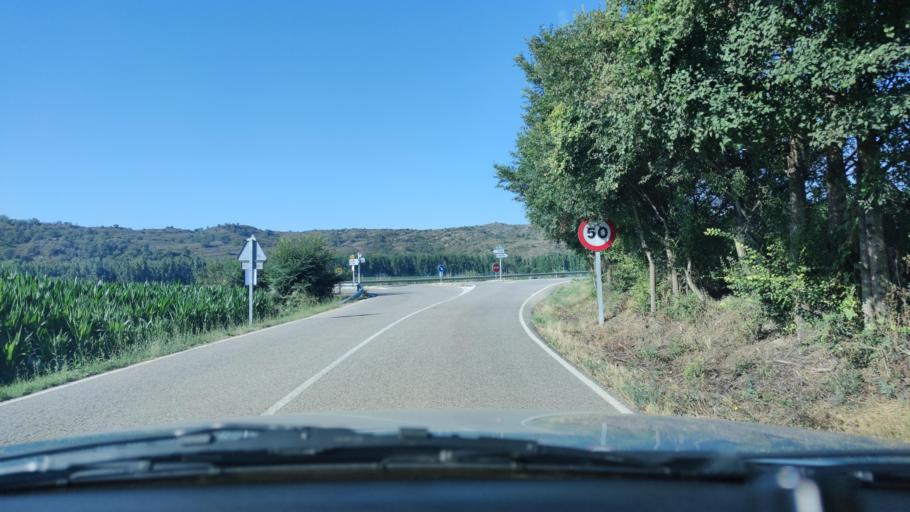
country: ES
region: Catalonia
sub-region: Provincia de Lleida
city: Ponts
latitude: 41.8907
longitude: 1.2317
